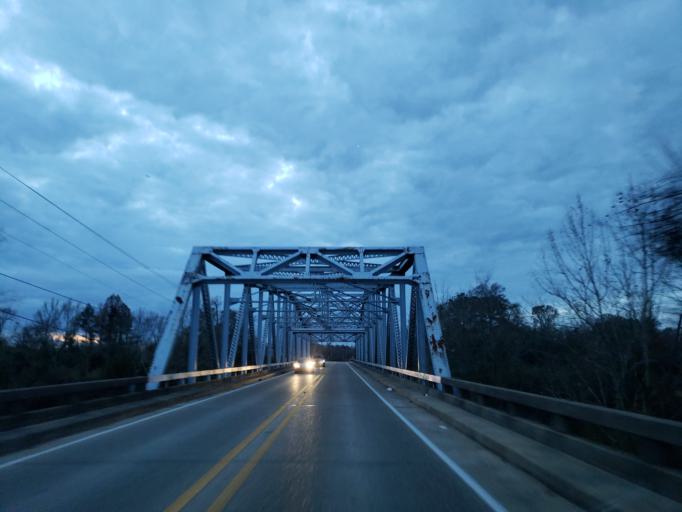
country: US
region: Mississippi
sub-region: Forrest County
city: Petal
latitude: 31.3270
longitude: -89.2666
